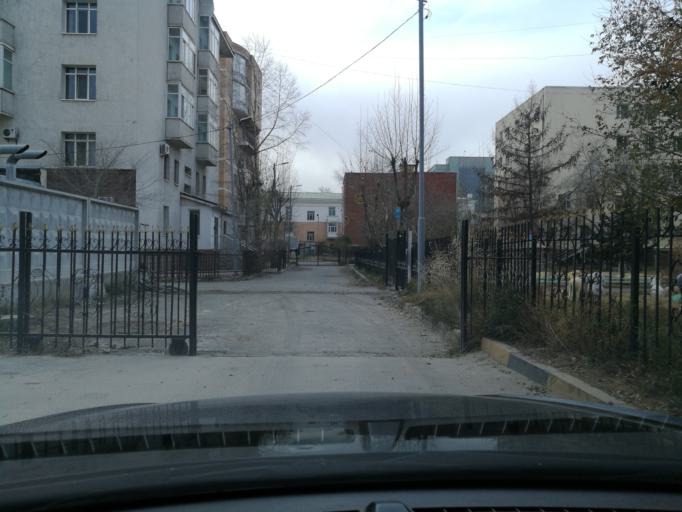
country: MN
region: Ulaanbaatar
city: Ulaanbaatar
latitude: 47.9231
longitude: 106.9173
